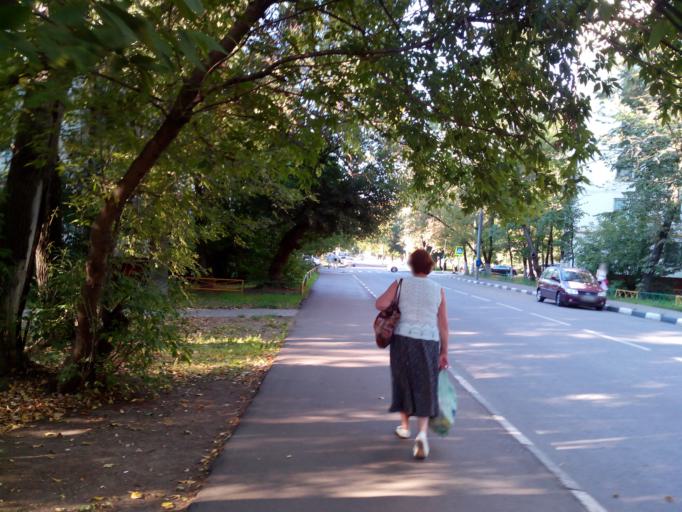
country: RU
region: Moscow
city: Novokuz'minki
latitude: 55.7207
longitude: 37.7956
